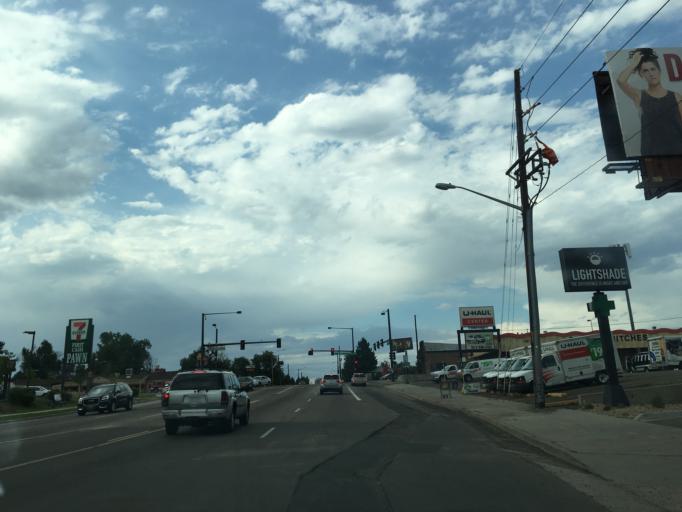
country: US
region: Colorado
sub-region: Jefferson County
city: Lakewood
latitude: 39.6958
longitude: -105.0531
